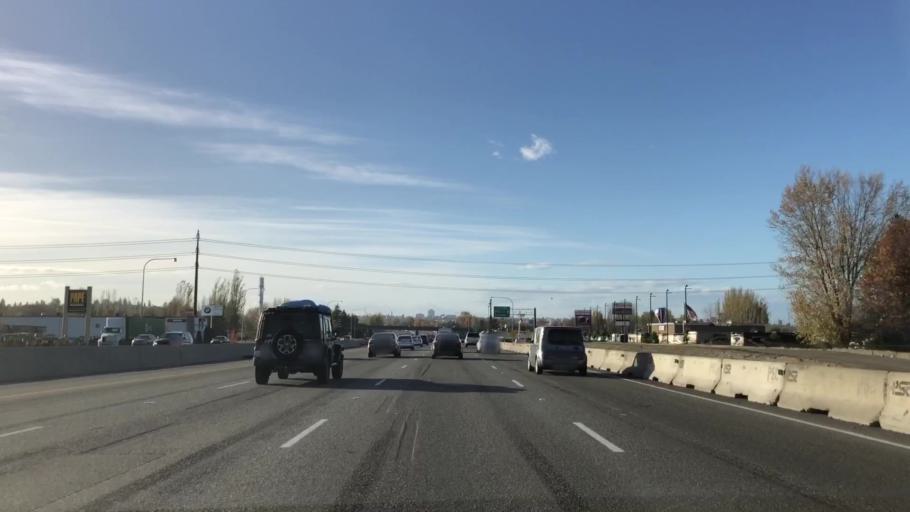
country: US
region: Washington
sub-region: Pierce County
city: Fife
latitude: 47.2411
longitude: -122.3783
